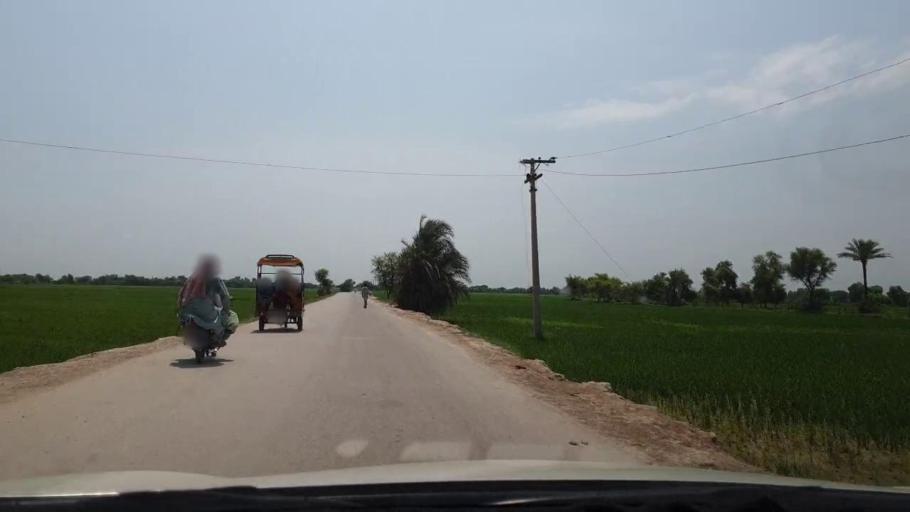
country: PK
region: Sindh
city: Ratodero
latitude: 27.8228
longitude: 68.2430
